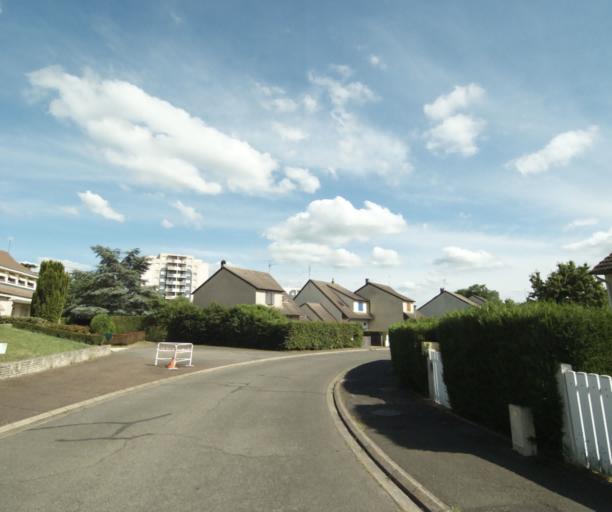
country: FR
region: Centre
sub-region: Departement d'Eure-et-Loir
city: Luce
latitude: 48.4360
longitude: 1.4520
